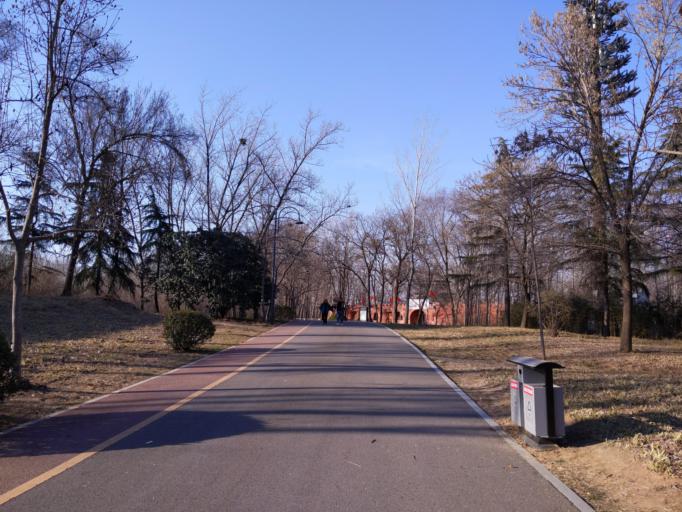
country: CN
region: Henan Sheng
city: Puyang
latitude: 35.7777
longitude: 114.9642
